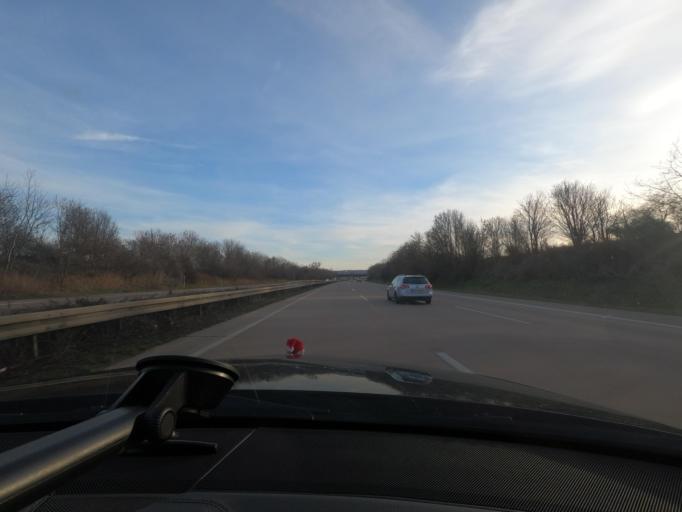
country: DE
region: Lower Saxony
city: Harsum
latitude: 52.1781
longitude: 9.9770
